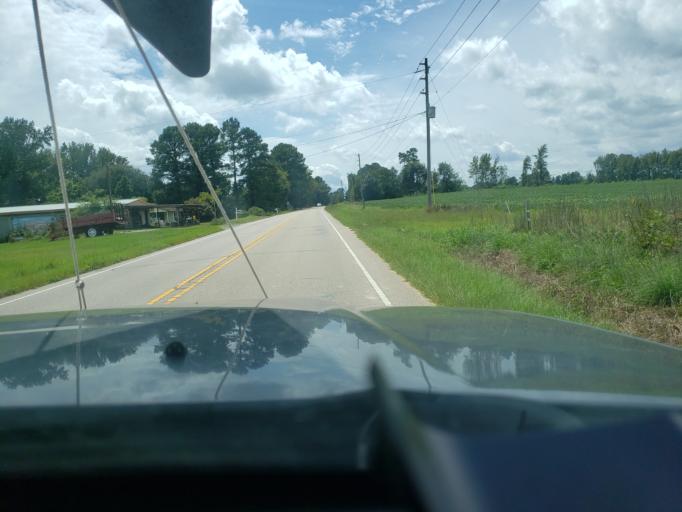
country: US
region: North Carolina
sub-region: Wake County
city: Rolesville
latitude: 35.8858
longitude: -78.4393
